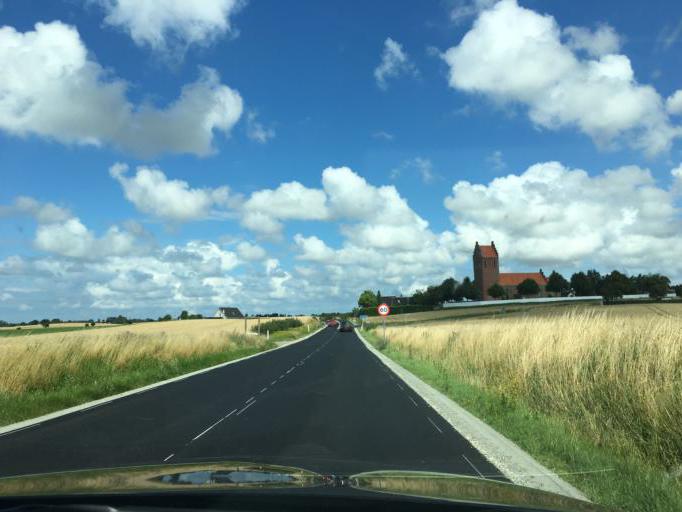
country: DK
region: Capital Region
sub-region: Gribskov Kommune
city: Helsinge
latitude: 56.0546
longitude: 12.1998
